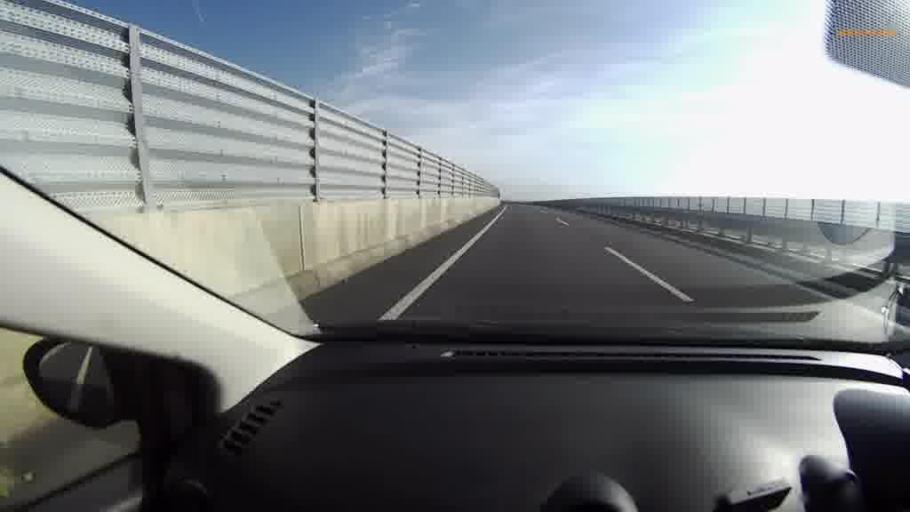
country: JP
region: Hokkaido
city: Kushiro
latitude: 43.0233
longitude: 144.2788
